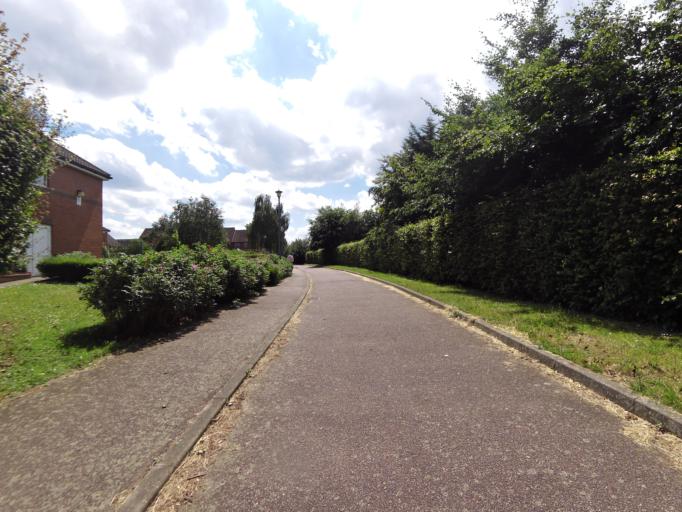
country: GB
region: England
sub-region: Suffolk
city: Ipswich
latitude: 52.0370
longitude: 1.1727
